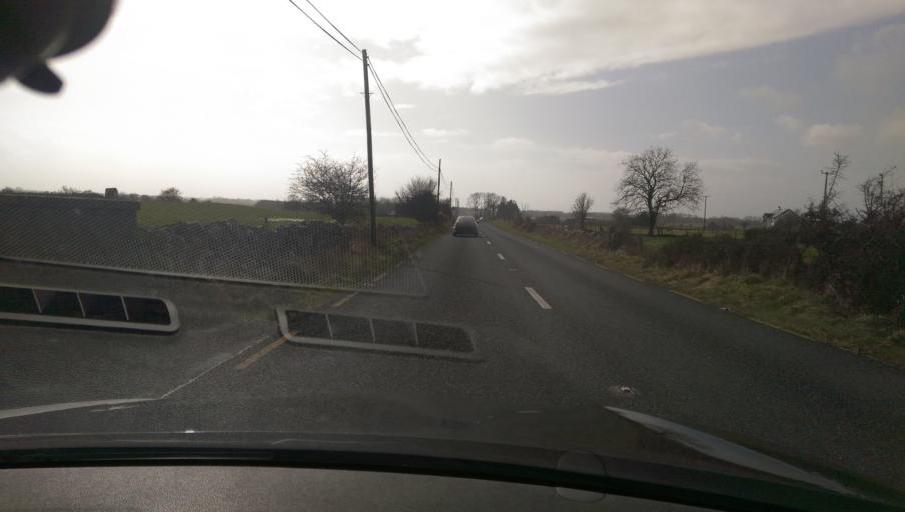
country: IE
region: Connaught
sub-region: County Galway
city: Athenry
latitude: 53.3586
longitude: -8.7350
